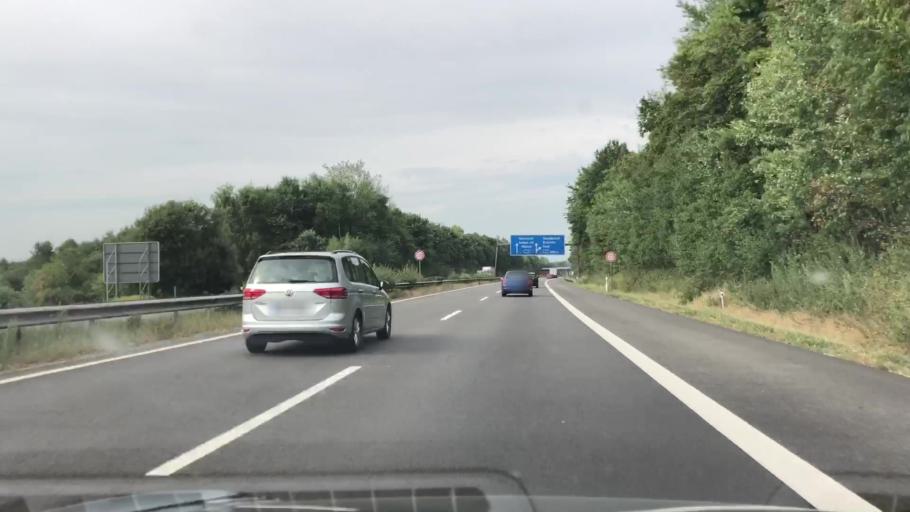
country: DE
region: Lower Saxony
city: Buchholz in der Nordheide
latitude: 53.3816
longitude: 9.8702
